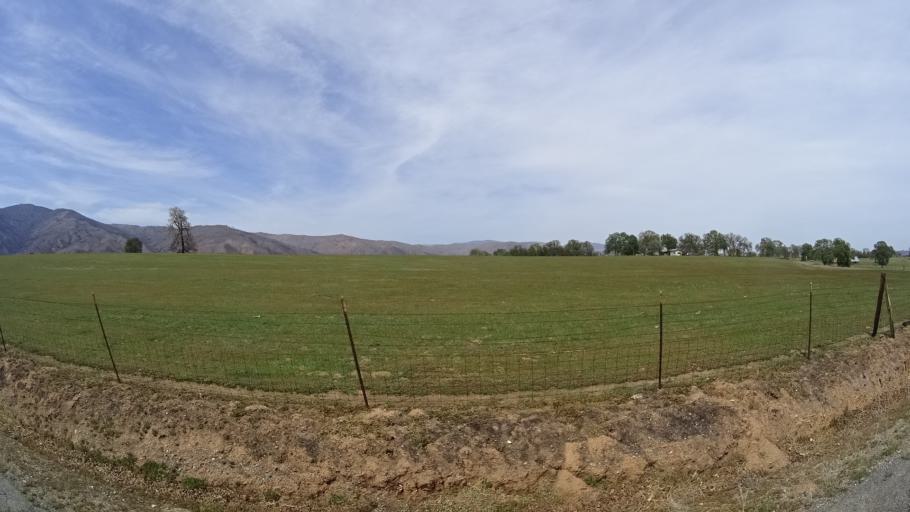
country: US
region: California
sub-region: Glenn County
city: Willows
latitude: 39.5856
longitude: -122.5784
